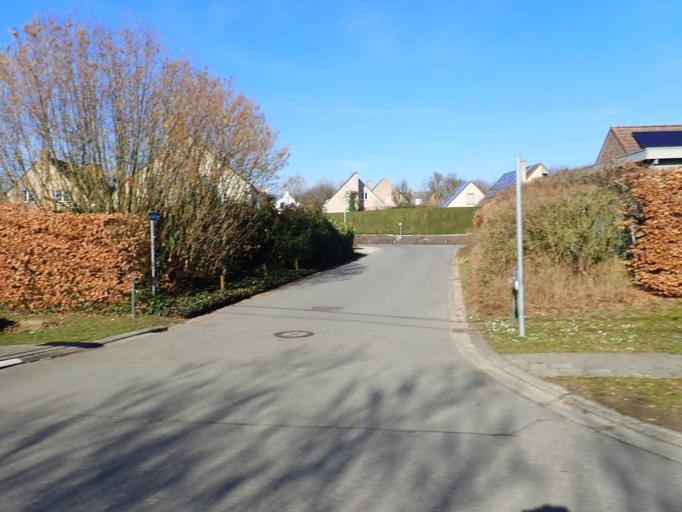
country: BE
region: Flanders
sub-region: Provincie Oost-Vlaanderen
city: Temse
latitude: 51.1257
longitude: 4.2312
